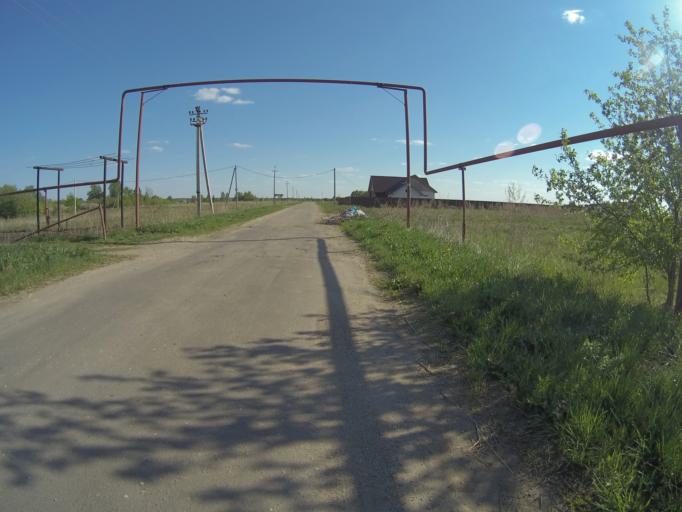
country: RU
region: Vladimir
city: Kideksha
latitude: 56.3811
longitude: 40.5595
